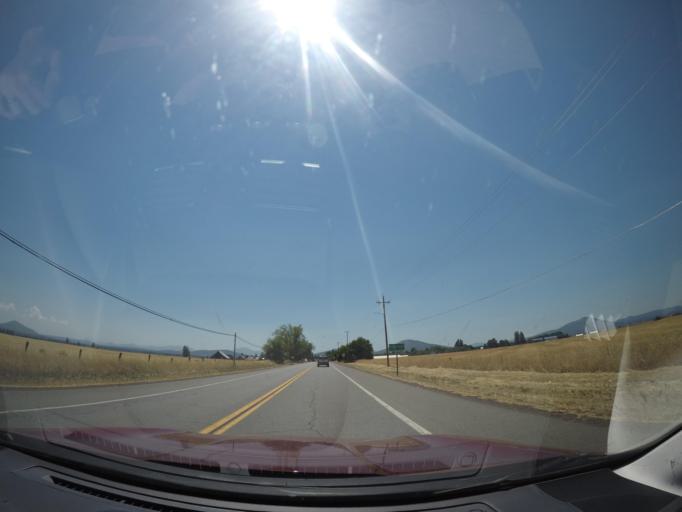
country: US
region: California
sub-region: Shasta County
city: Burney
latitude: 41.0537
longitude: -121.3907
